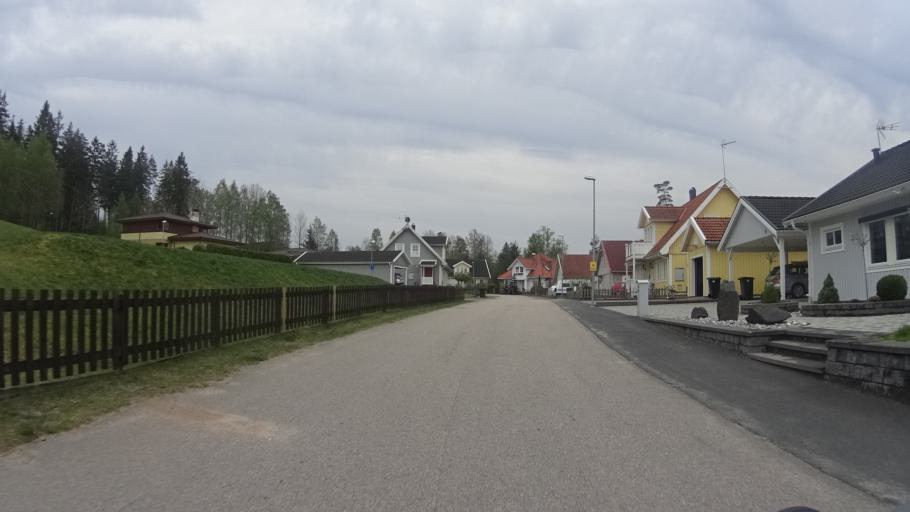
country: SE
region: Kronoberg
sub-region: Ljungby Kommun
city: Ljungby
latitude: 56.8367
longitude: 13.9729
